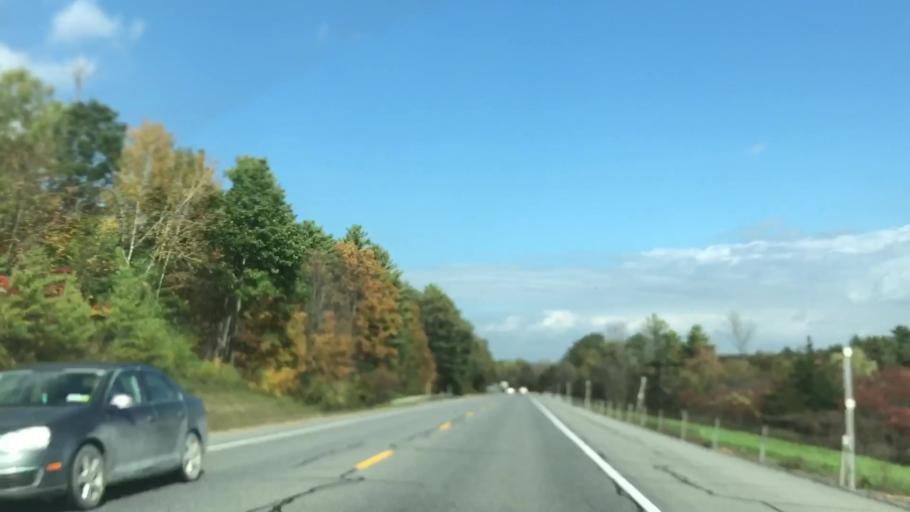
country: US
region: New York
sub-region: Washington County
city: Whitehall
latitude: 43.4408
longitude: -73.4560
